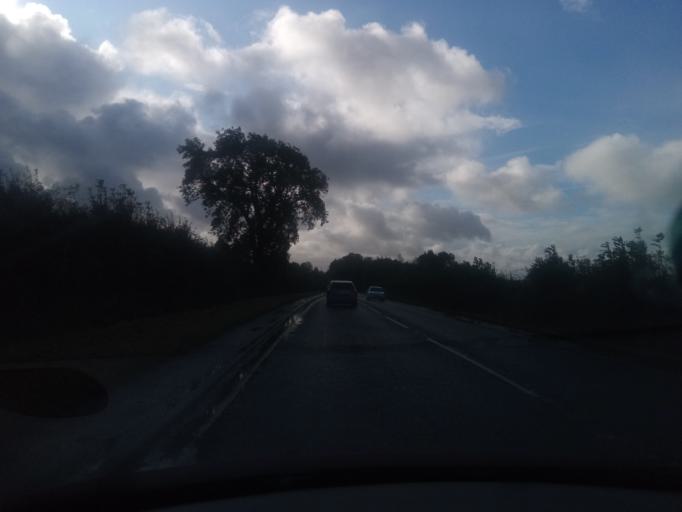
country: GB
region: England
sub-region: Cumbria
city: Carlisle
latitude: 54.9479
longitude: -2.9433
